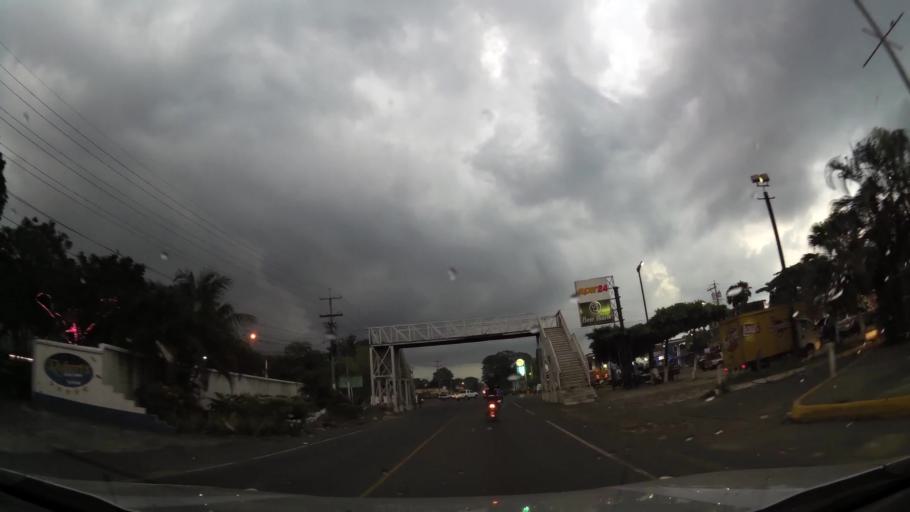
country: GT
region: Escuintla
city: Santa Lucia Cotzumalguapa
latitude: 14.3297
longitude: -91.0192
